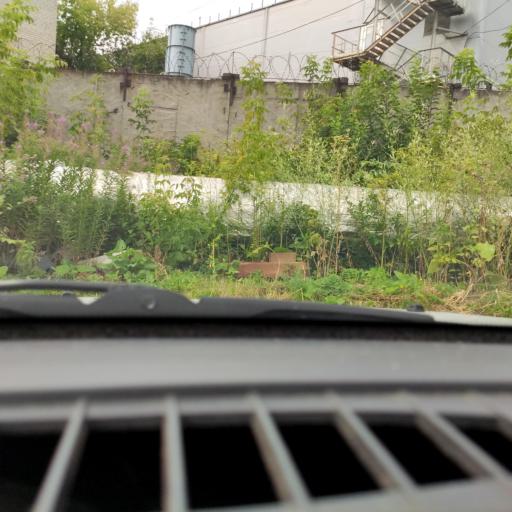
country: RU
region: Perm
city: Perm
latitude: 57.9828
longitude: 56.2626
